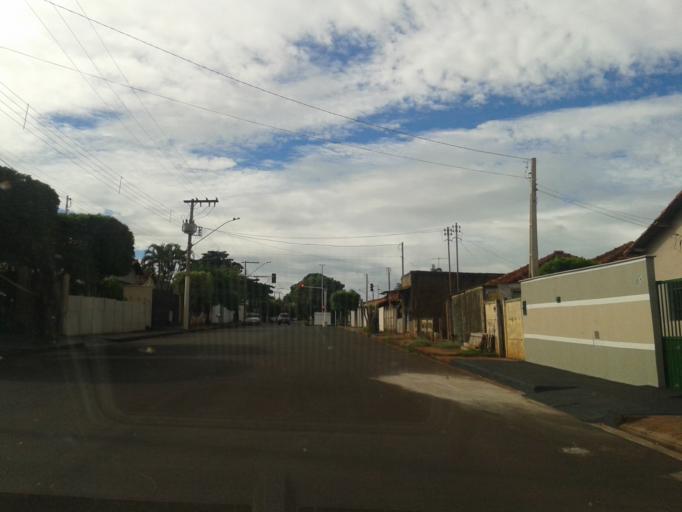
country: BR
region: Minas Gerais
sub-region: Ituiutaba
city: Ituiutaba
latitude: -18.9832
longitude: -49.4690
